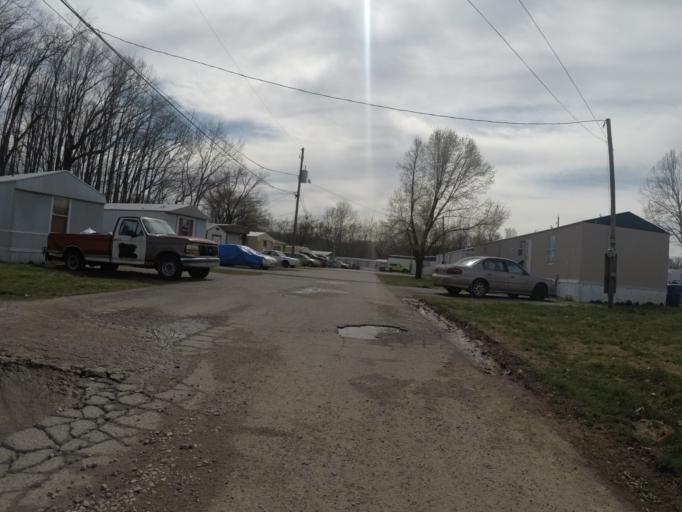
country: US
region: West Virginia
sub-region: Cabell County
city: Pea Ridge
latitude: 38.4191
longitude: -82.3457
